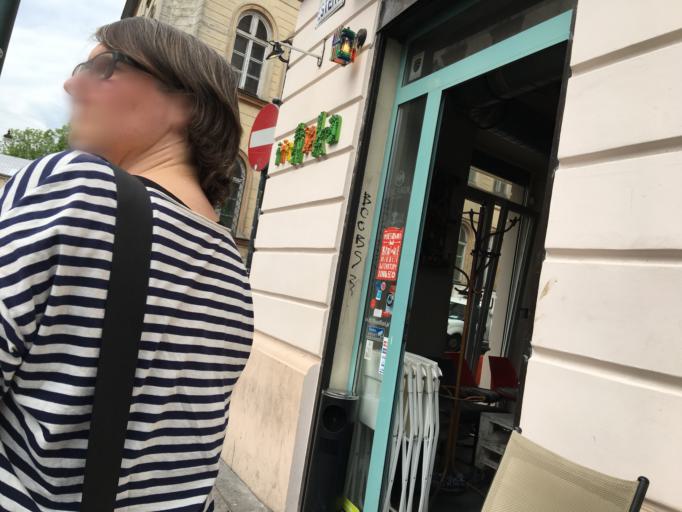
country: PL
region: Lesser Poland Voivodeship
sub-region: Krakow
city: Krakow
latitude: 50.0521
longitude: 19.9452
